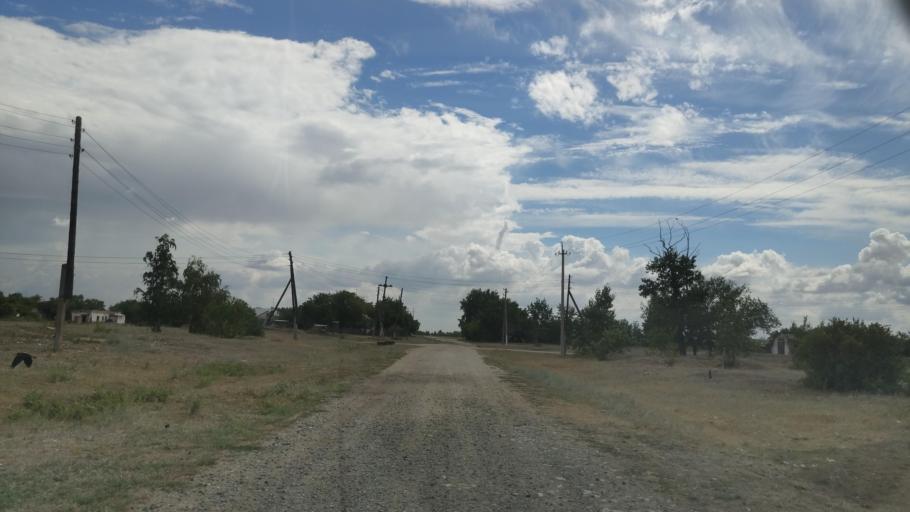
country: KZ
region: Pavlodar
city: Pavlodar
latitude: 52.6499
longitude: 77.0225
